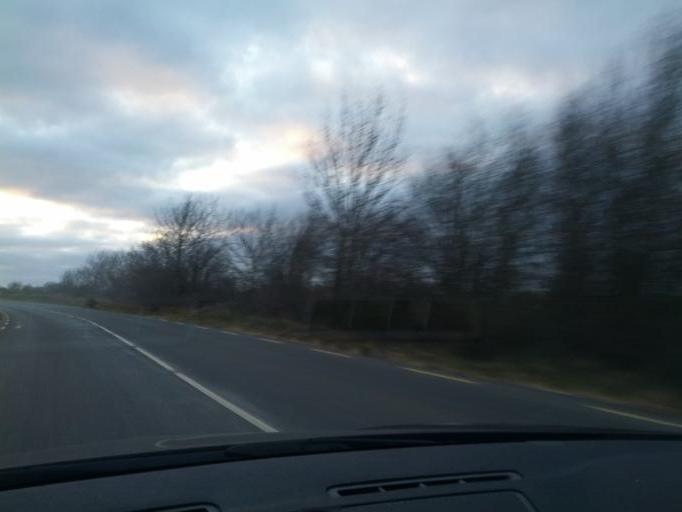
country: IE
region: Leinster
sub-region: Uibh Fhaili
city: Banagher
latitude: 53.1067
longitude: -8.0365
